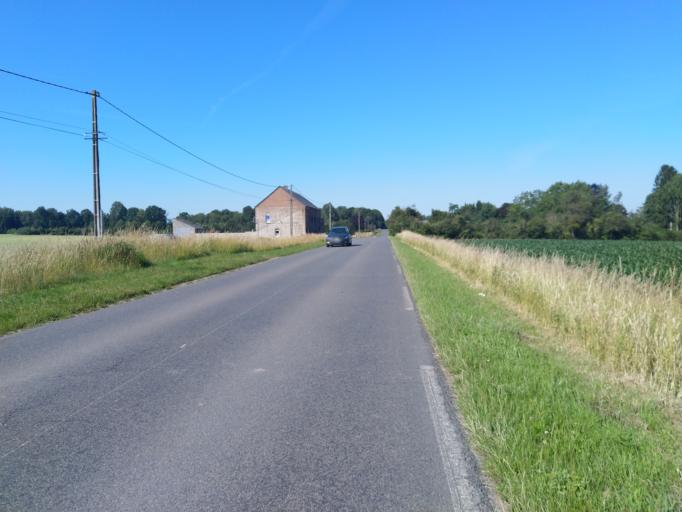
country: FR
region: Nord-Pas-de-Calais
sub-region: Departement du Nord
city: Feignies
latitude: 50.3333
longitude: 3.9221
